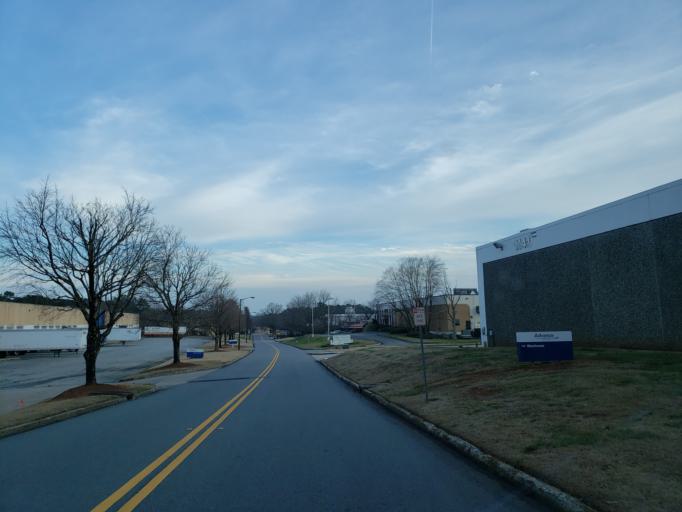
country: US
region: Georgia
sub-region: Cobb County
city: Marietta
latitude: 33.9802
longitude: -84.5350
